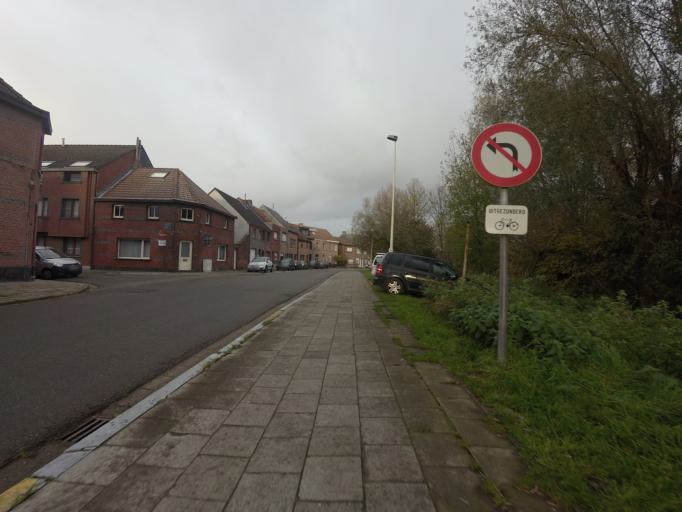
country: BE
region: Flanders
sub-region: Provincie Antwerpen
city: Niel
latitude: 51.1081
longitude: 4.3326
